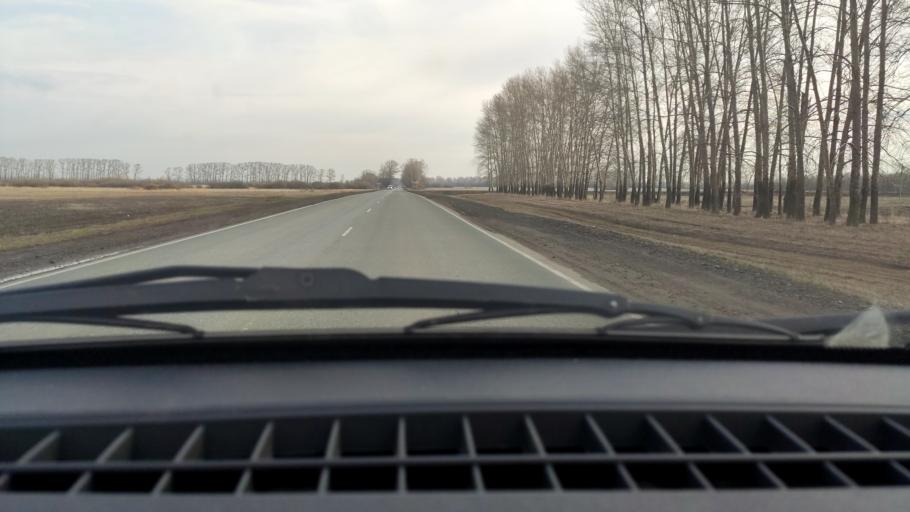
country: RU
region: Bashkortostan
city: Chishmy
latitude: 54.3965
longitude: 55.2085
